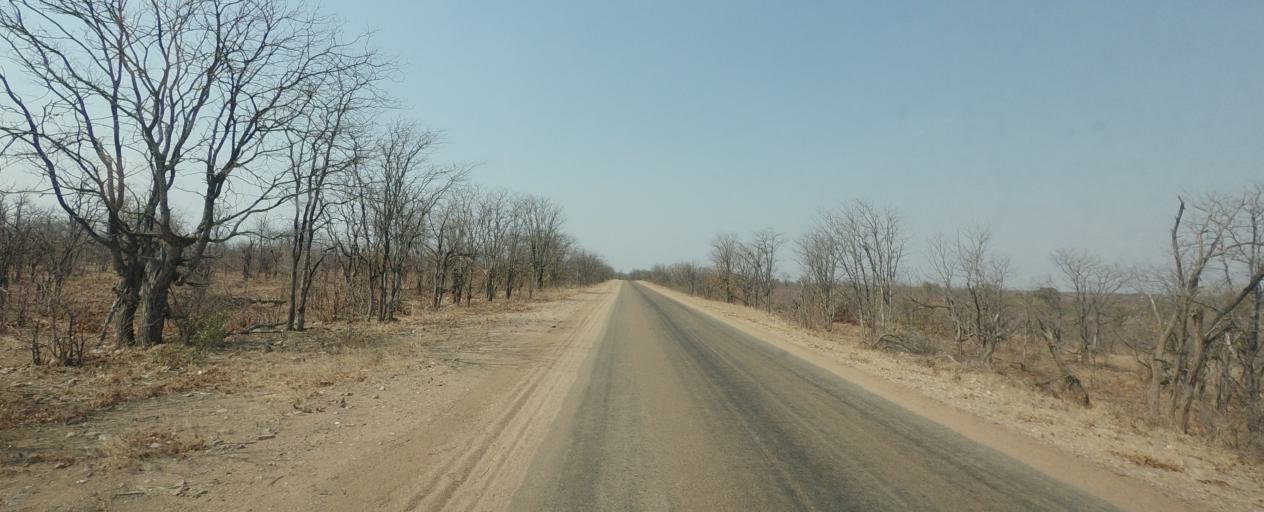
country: ZA
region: Limpopo
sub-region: Mopani District Municipality
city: Giyani
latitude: -23.1943
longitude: 31.3132
